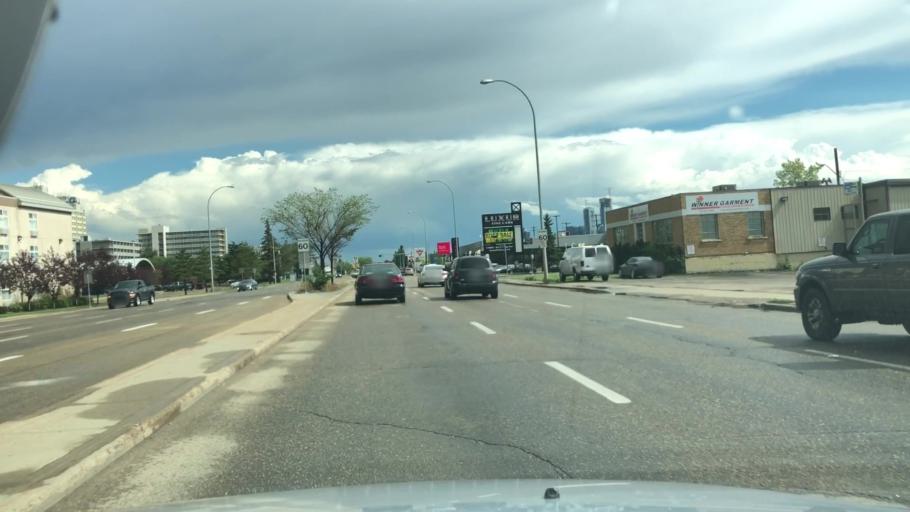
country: CA
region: Alberta
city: Edmonton
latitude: 53.5698
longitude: -113.5296
